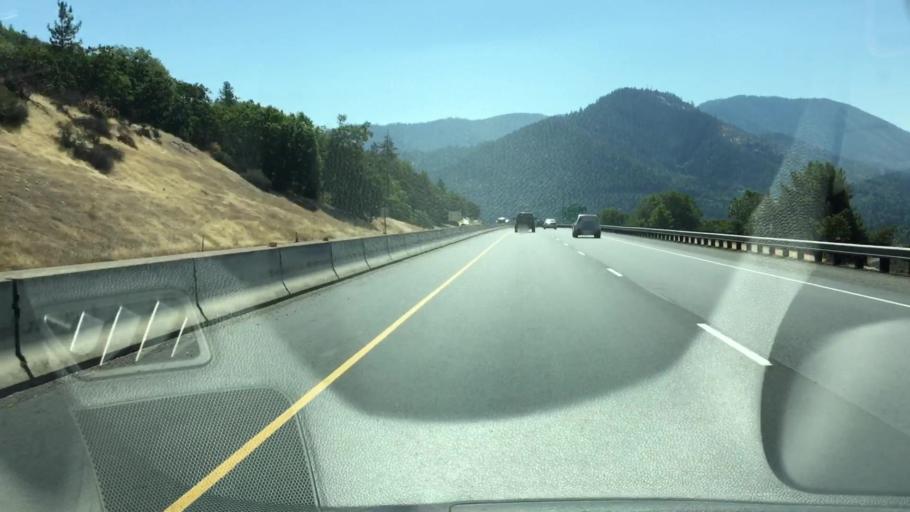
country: US
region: Oregon
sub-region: Josephine County
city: Fruitdale
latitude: 42.4458
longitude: -123.3023
